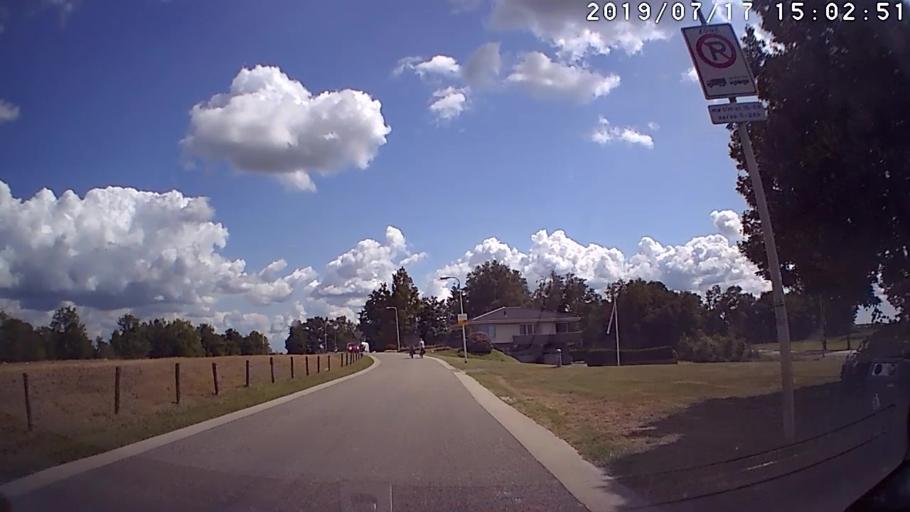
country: NL
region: Overijssel
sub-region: Gemeente Kampen
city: Kampen
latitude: 52.5182
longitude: 5.9567
